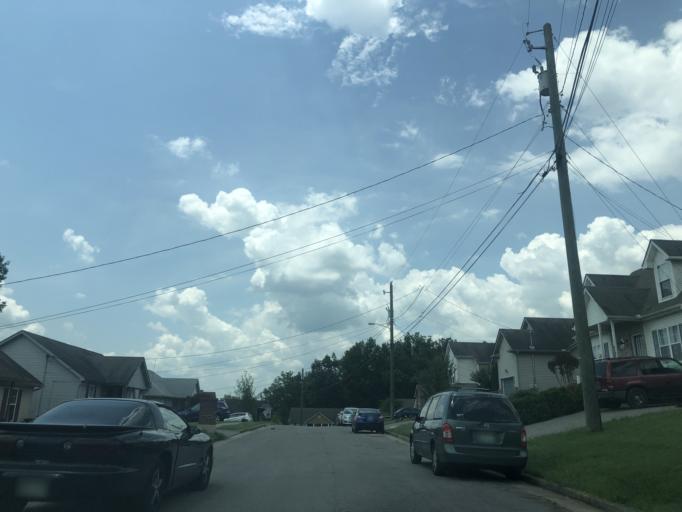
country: US
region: Tennessee
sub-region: Rutherford County
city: La Vergne
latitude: 36.0591
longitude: -86.6568
